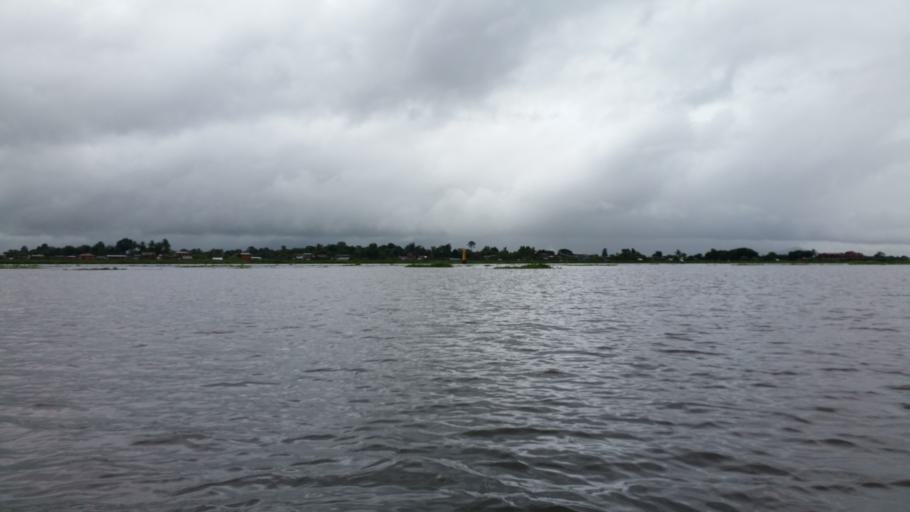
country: MM
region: Shan
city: Taunggyi
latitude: 20.5299
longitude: 96.9001
